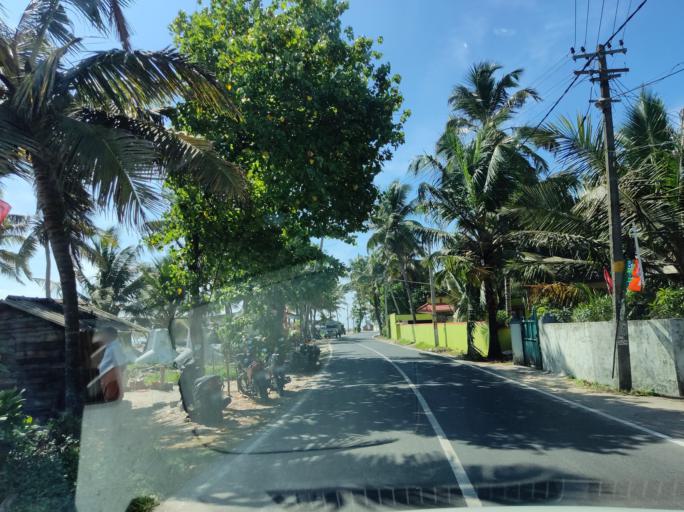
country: IN
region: Kerala
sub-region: Alappuzha
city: Kayankulam
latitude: 9.2065
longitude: 76.4317
